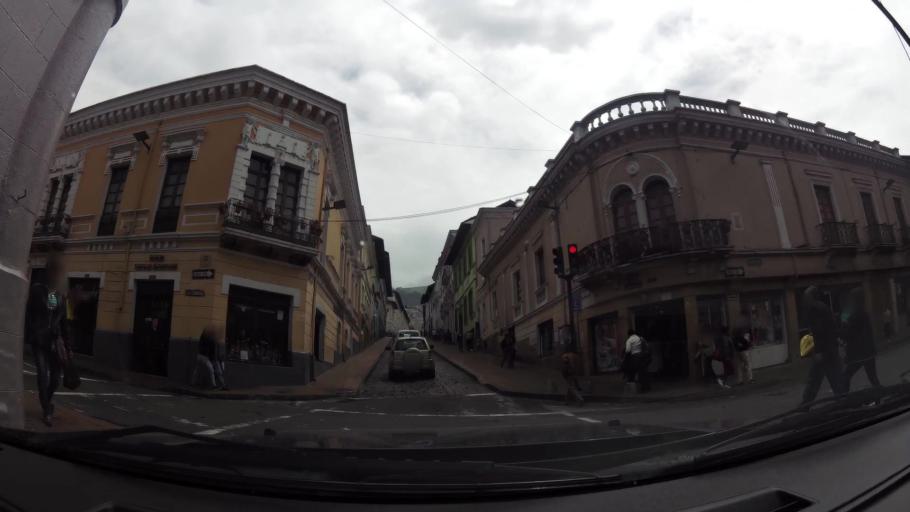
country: EC
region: Pichincha
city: Quito
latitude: -0.2187
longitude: -78.5104
